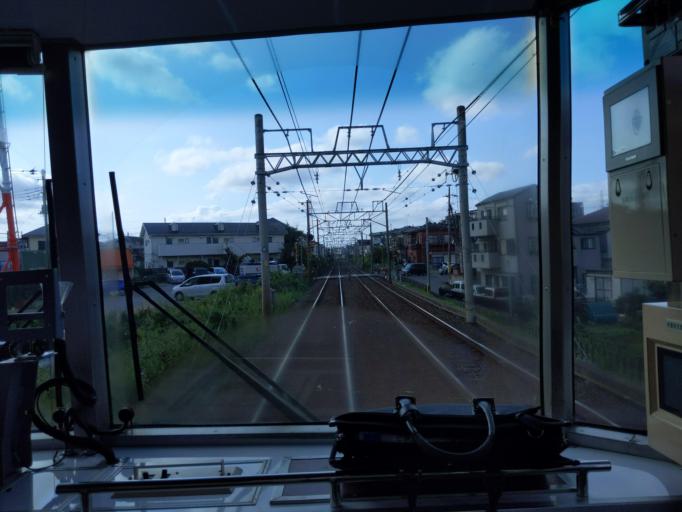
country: JP
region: Chiba
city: Shiroi
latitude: 35.7547
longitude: 140.0219
